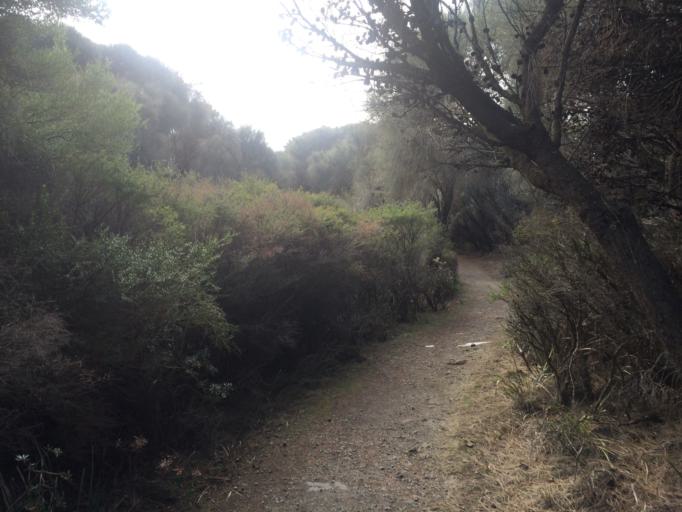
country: AU
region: Victoria
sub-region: Colac-Otway
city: Apollo Bay
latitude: -38.7580
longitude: 143.2223
